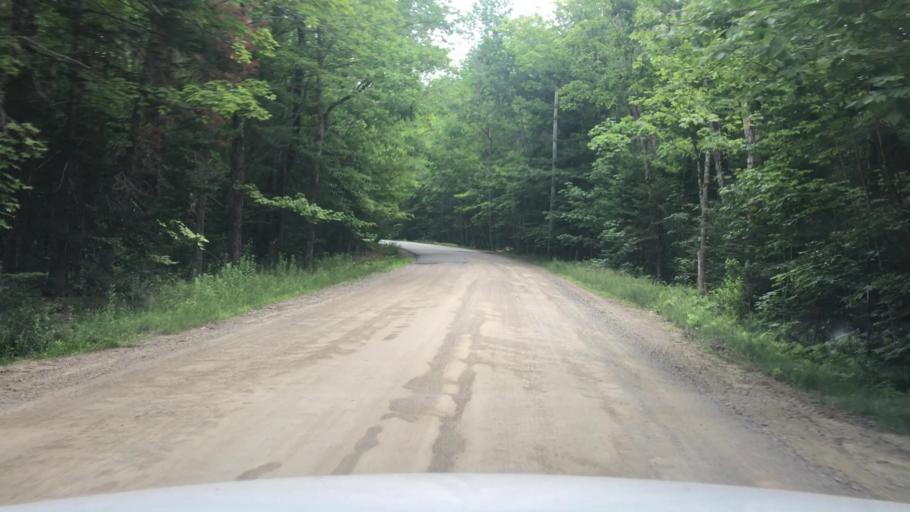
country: US
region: Maine
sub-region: Kennebec County
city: Albion
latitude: 44.4547
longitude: -69.3210
